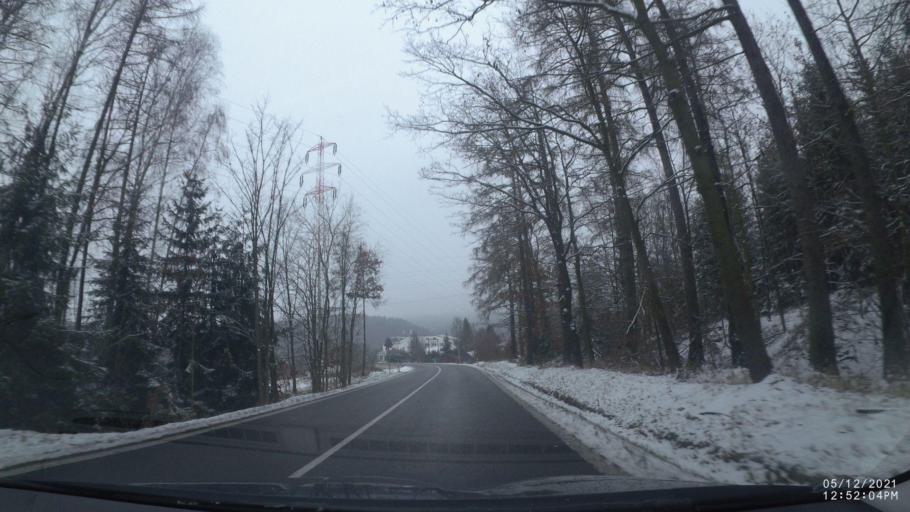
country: CZ
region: Kralovehradecky
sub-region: Okres Nachod
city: Nachod
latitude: 50.4039
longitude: 16.1390
